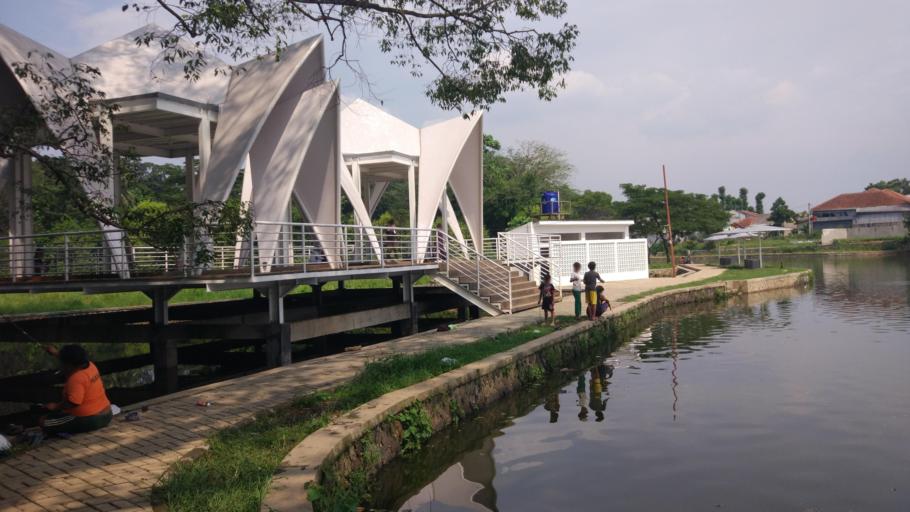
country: ID
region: West Java
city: Ciampea
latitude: -6.5529
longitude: 106.7484
